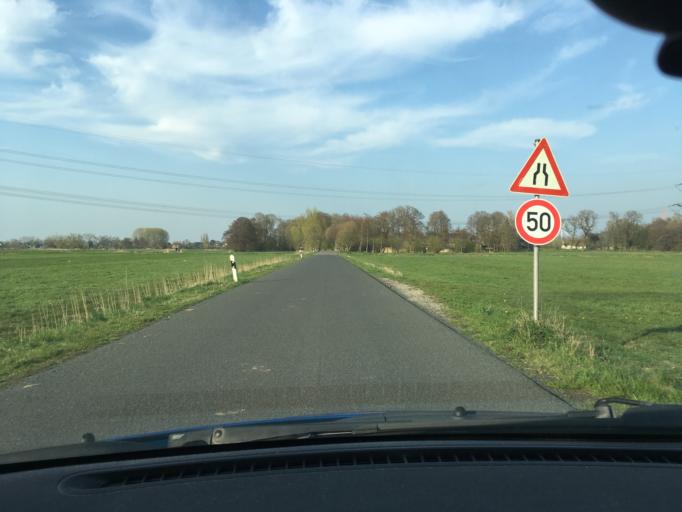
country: DE
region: Lower Saxony
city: Stelle
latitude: 53.4431
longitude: 10.0624
